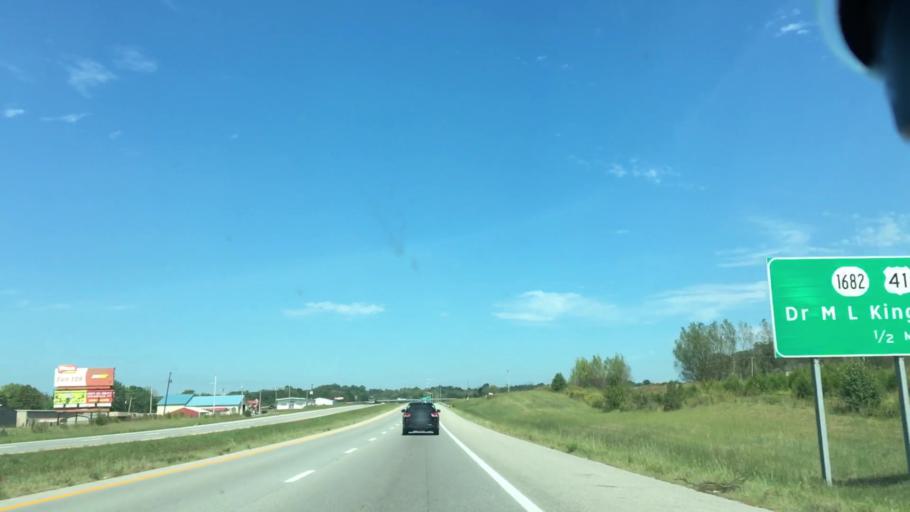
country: US
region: Kentucky
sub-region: Christian County
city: Hopkinsville
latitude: 36.8874
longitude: -87.4687
